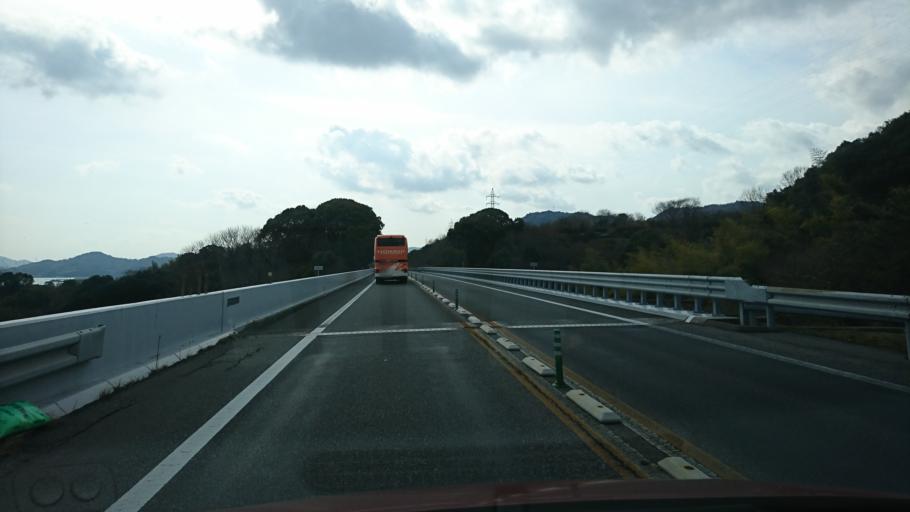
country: JP
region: Hiroshima
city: Innoshima
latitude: 34.2444
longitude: 133.0479
